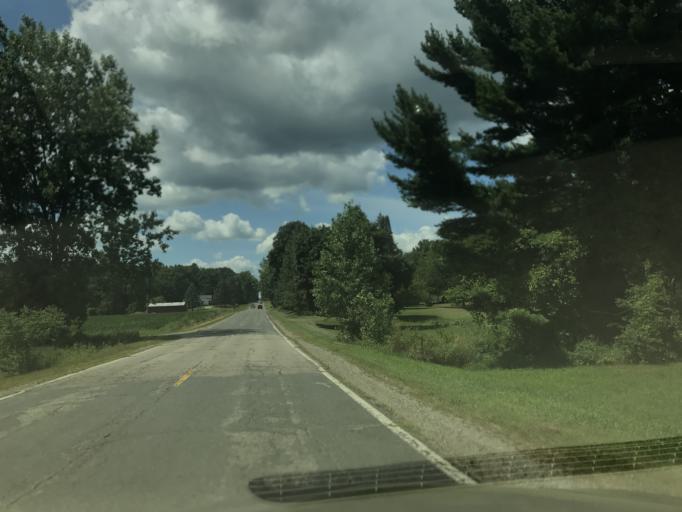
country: US
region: Michigan
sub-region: Ingham County
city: Leslie
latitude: 42.4509
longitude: -84.5407
